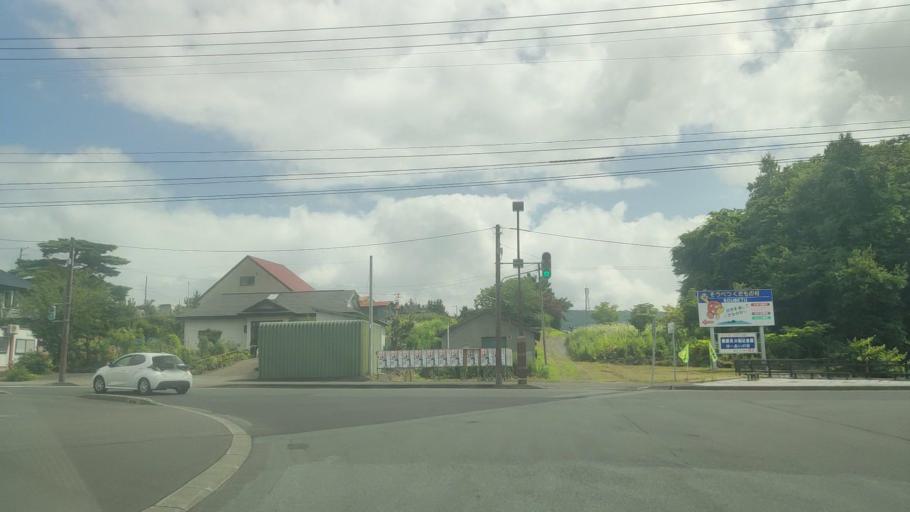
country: JP
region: Hokkaido
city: Date
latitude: 42.5574
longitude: 140.8876
